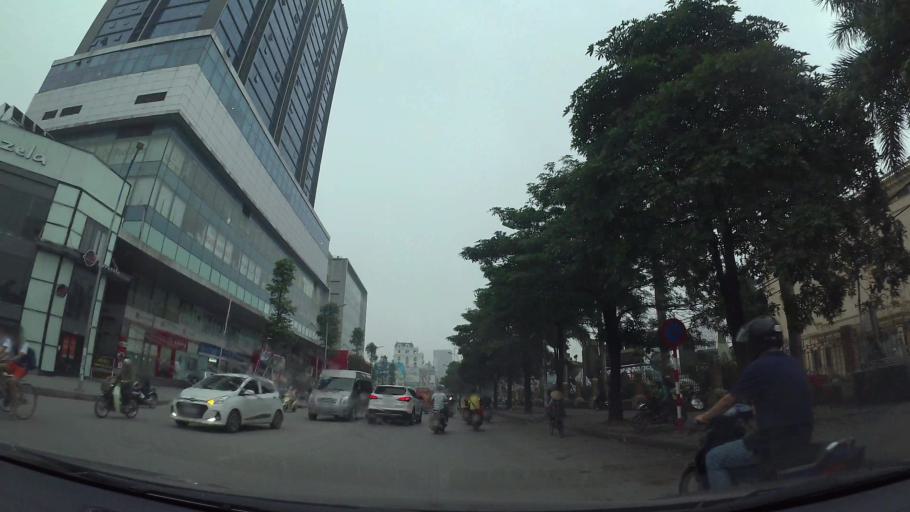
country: VN
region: Ha Noi
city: Dong Da
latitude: 20.9989
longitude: 105.8286
